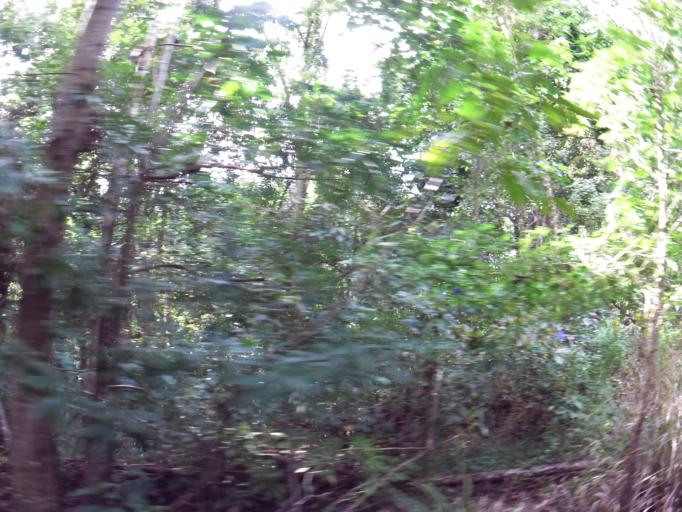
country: AU
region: Queensland
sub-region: Cairns
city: Redlynch
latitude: -16.8795
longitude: 145.6549
